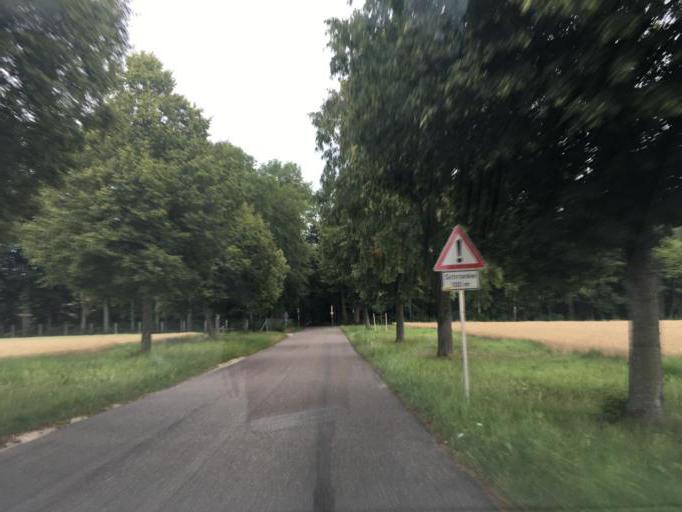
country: DE
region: Baden-Wuerttemberg
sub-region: Tuebingen Region
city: Kirchentellinsfurt
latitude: 48.5457
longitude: 9.1350
